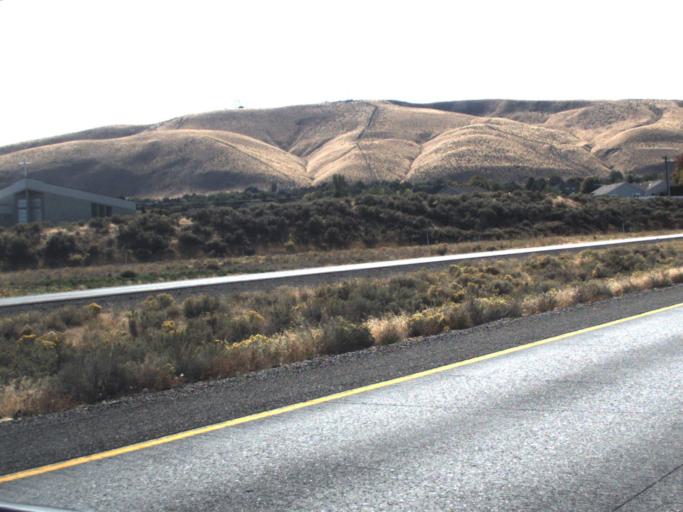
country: US
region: Washington
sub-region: Benton County
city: Richland
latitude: 46.2539
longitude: -119.3066
